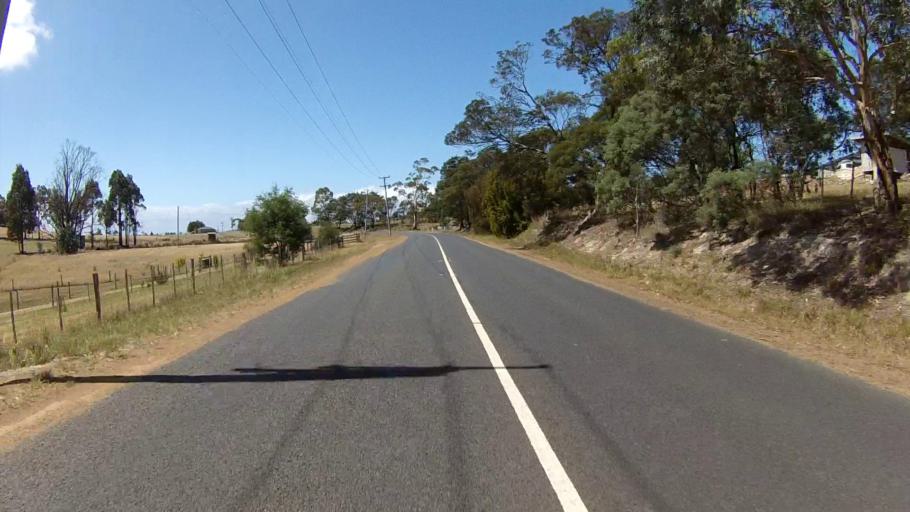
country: AU
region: Tasmania
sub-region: Clarence
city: Sandford
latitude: -42.9571
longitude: 147.4760
